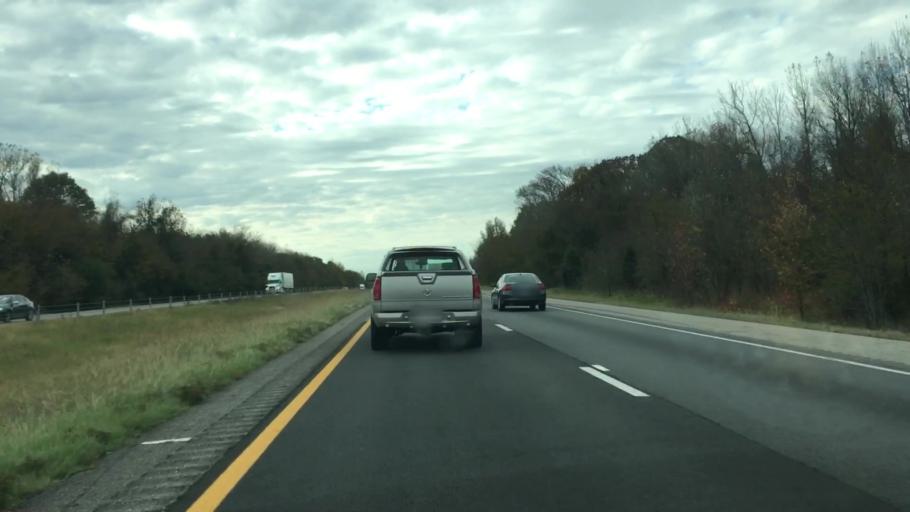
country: US
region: Arkansas
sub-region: Conway County
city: Morrilton
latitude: 35.1622
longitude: -92.6103
